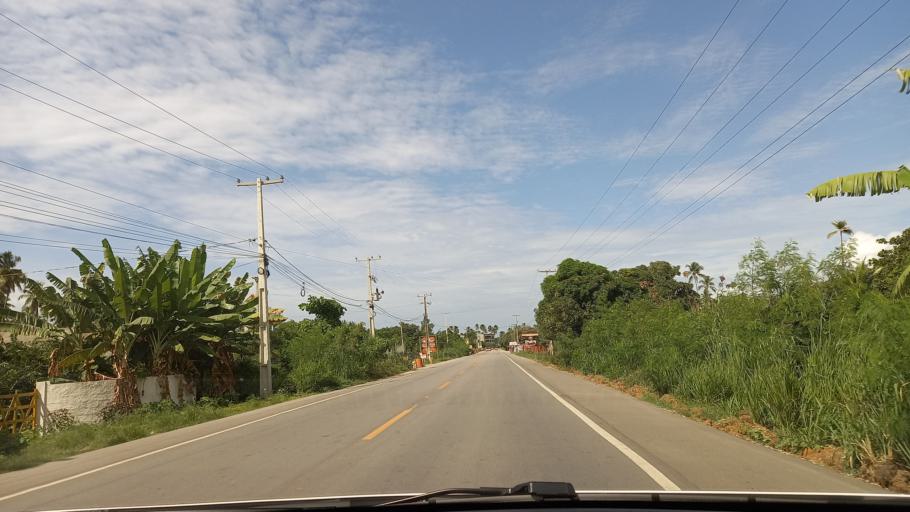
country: BR
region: Alagoas
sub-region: Maragogi
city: Maragogi
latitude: -8.9730
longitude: -35.1836
